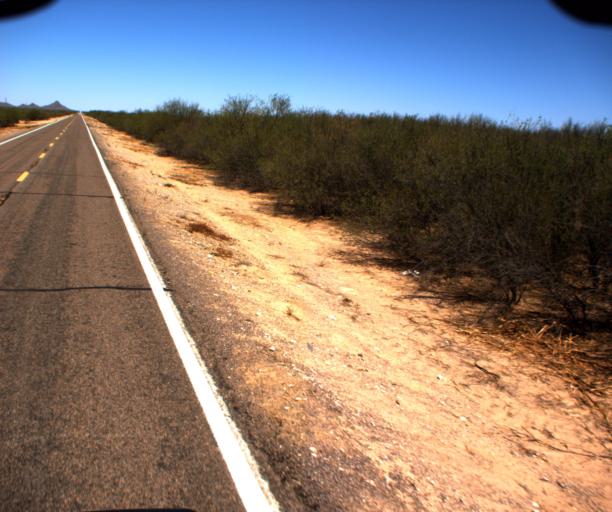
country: US
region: Arizona
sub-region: Pima County
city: Ajo
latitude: 32.1930
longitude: -112.4342
